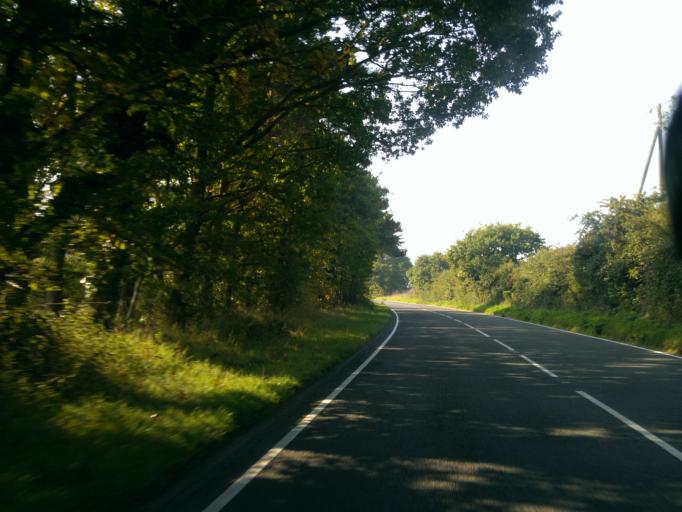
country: GB
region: England
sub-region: Essex
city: Eight Ash Green
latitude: 51.8590
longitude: 0.8215
